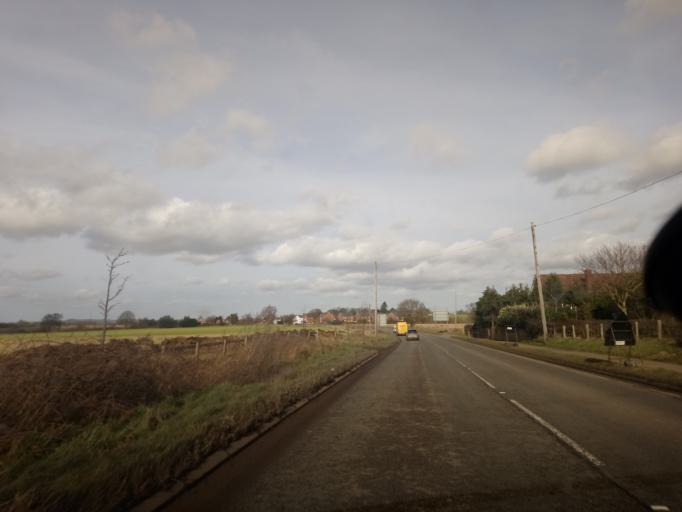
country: GB
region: England
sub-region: Telford and Wrekin
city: Eyton upon the Weald Moors
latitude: 52.7648
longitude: -2.5462
